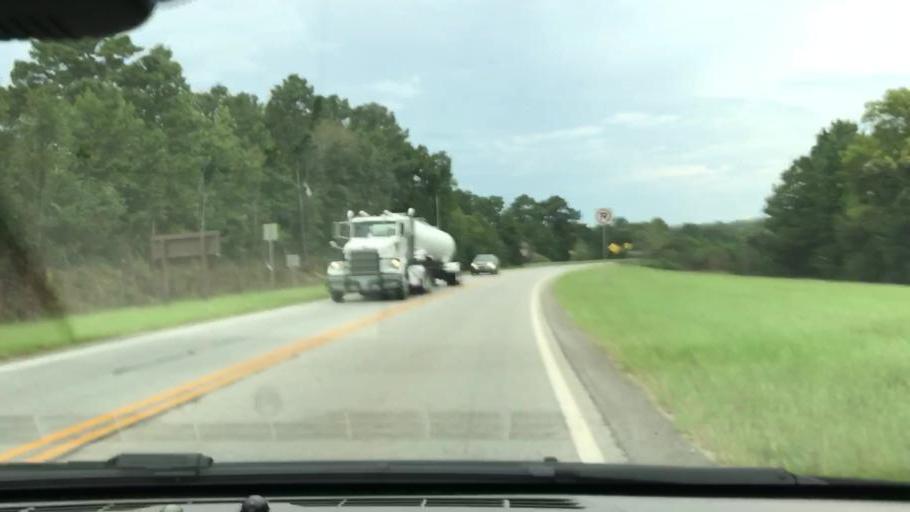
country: US
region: Alabama
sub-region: Houston County
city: Ashford
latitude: 31.2808
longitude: -85.0968
